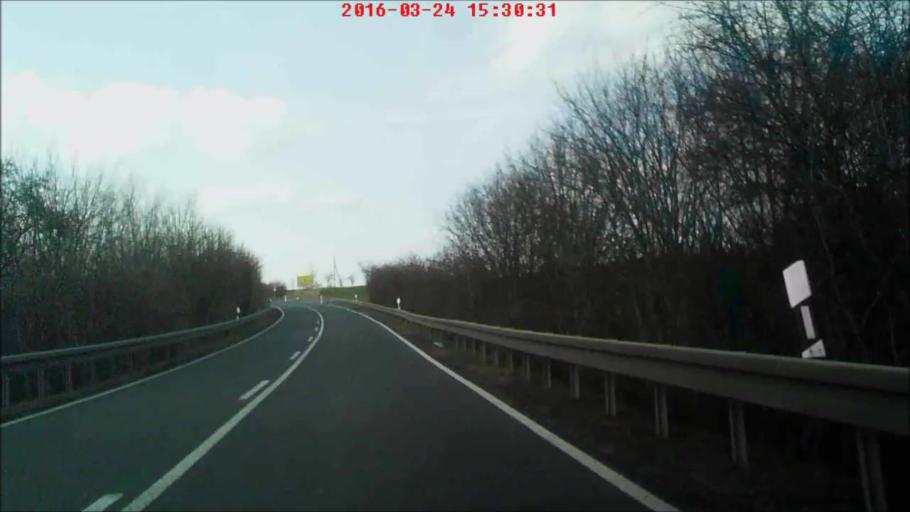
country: DE
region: Thuringia
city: Rockhausen
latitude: 50.8997
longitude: 11.0623
